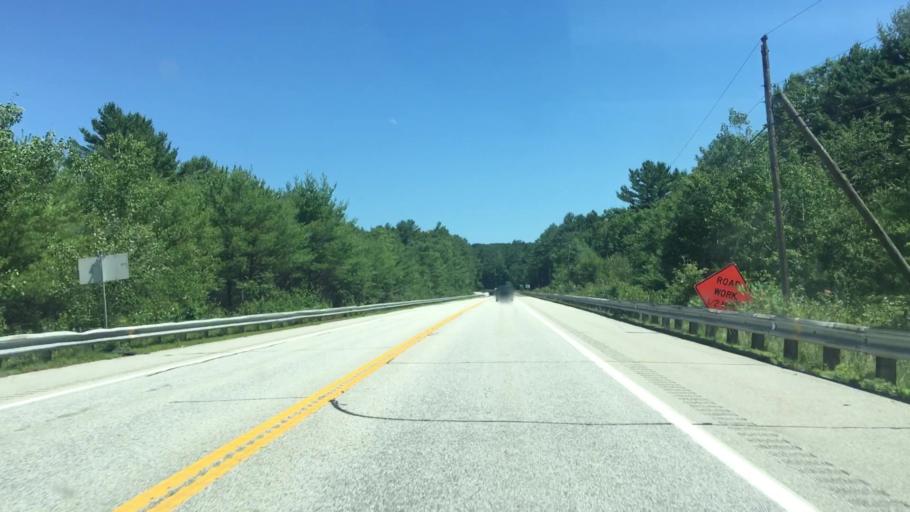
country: US
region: New Hampshire
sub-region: Merrimack County
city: Hopkinton
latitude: 43.1791
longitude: -71.7044
